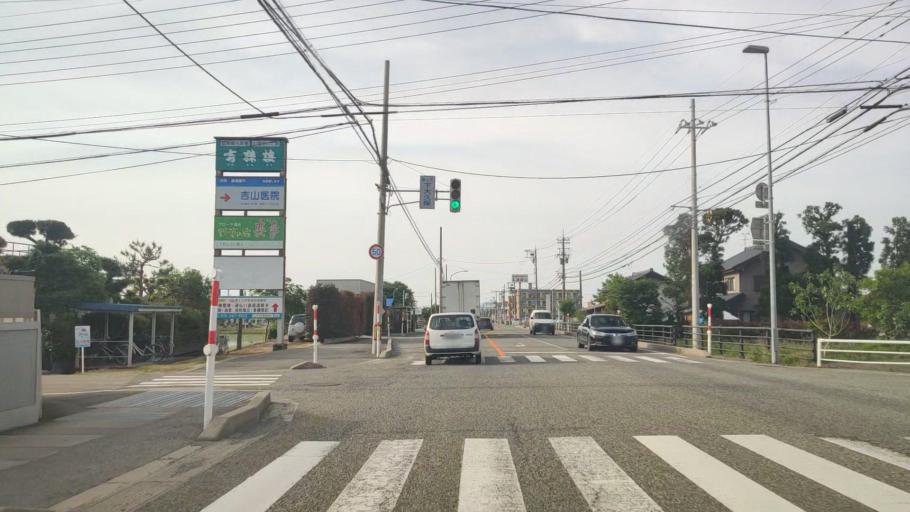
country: JP
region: Toyama
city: Yatsuomachi-higashikumisaka
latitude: 36.6101
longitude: 137.2045
